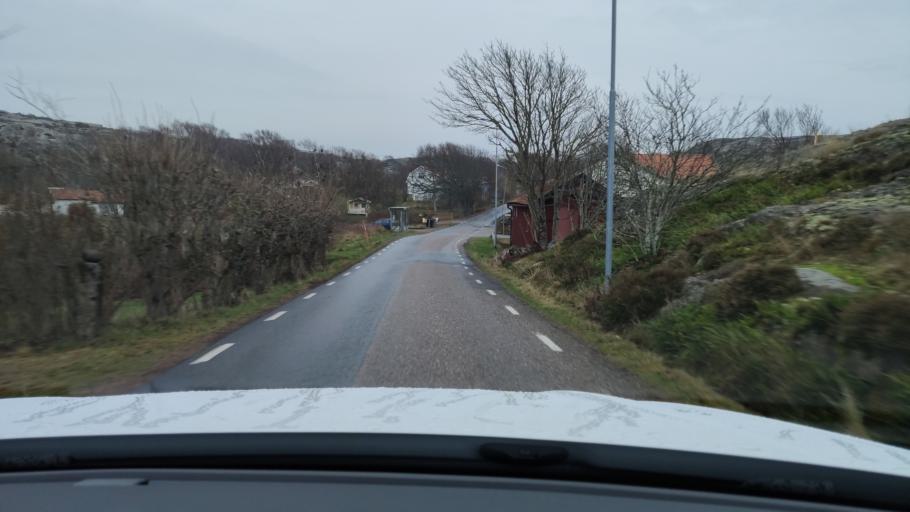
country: SE
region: Vaestra Goetaland
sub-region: Lysekils Kommun
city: Lysekil
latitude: 58.3228
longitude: 11.4089
